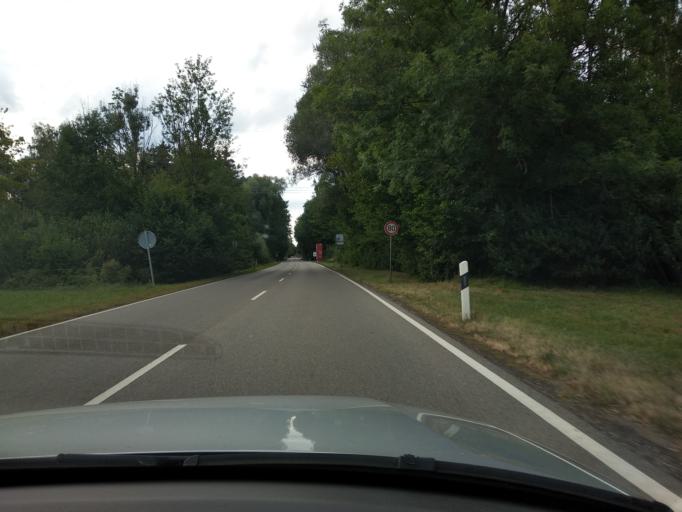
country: DE
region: Bavaria
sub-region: Swabia
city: Benningen
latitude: 47.9789
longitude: 10.2031
